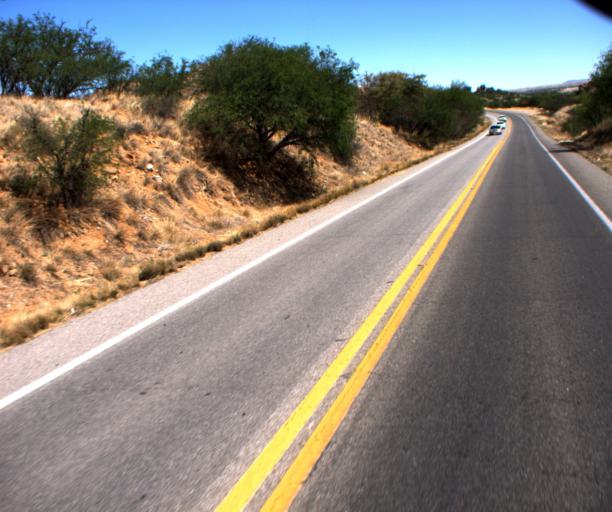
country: US
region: Arizona
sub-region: Santa Cruz County
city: Nogales
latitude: 31.3777
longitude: -110.8861
